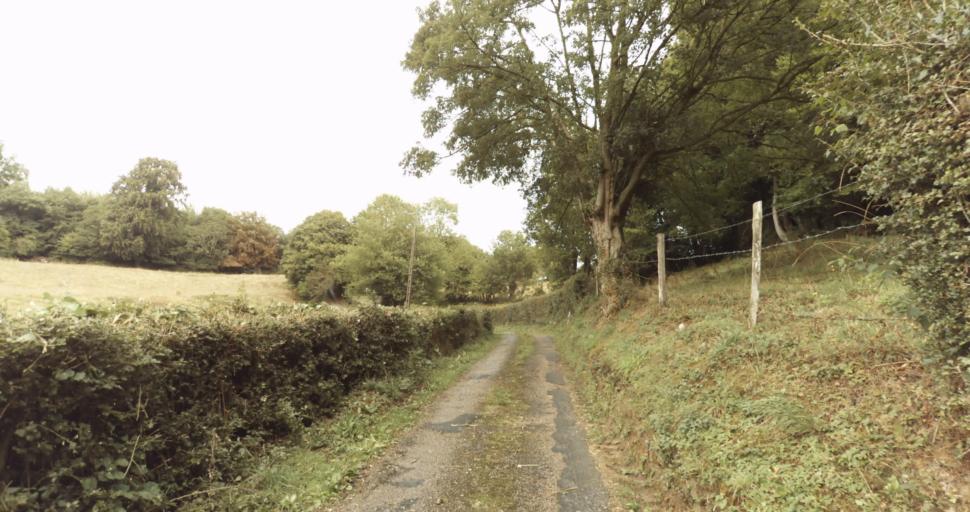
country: FR
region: Lower Normandy
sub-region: Departement de l'Orne
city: Vimoutiers
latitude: 48.8640
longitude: 0.1796
